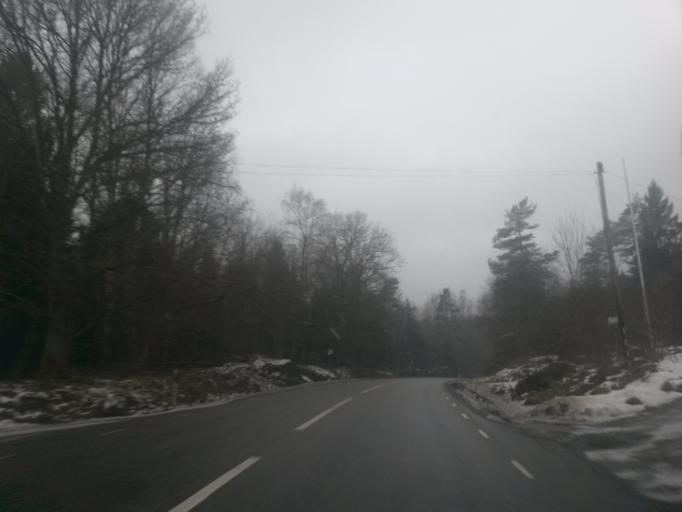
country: SE
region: Vaestra Goetaland
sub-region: Alingsas Kommun
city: Sollebrunn
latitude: 58.1137
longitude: 12.5630
